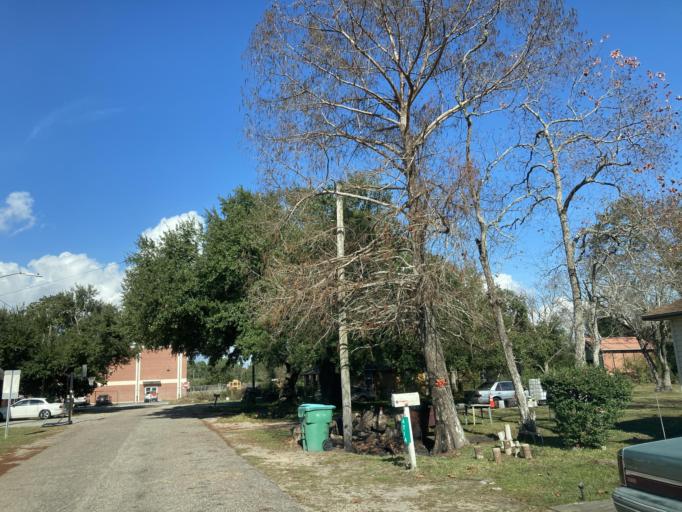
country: US
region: Mississippi
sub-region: Harrison County
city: West Gulfport
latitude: 30.4050
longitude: -89.0993
